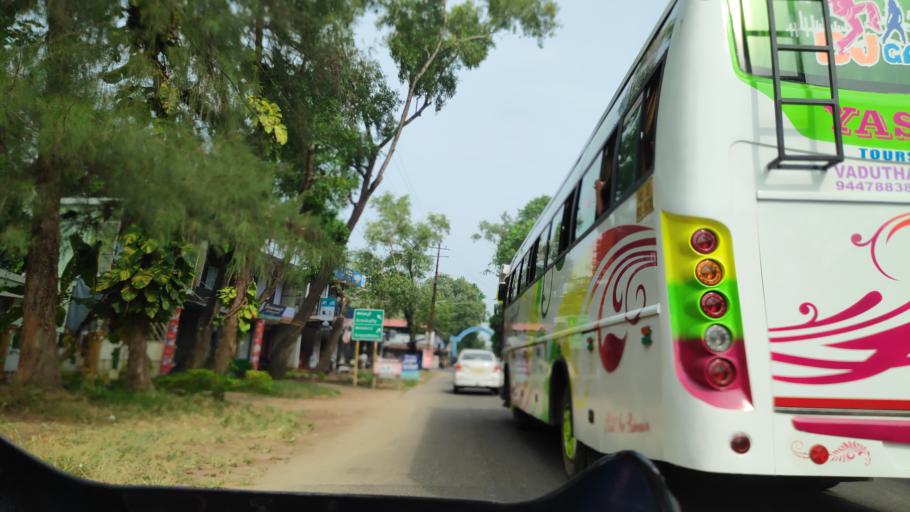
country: IN
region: Kerala
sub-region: Alappuzha
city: Kutiatodu
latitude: 9.8203
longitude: 76.3504
